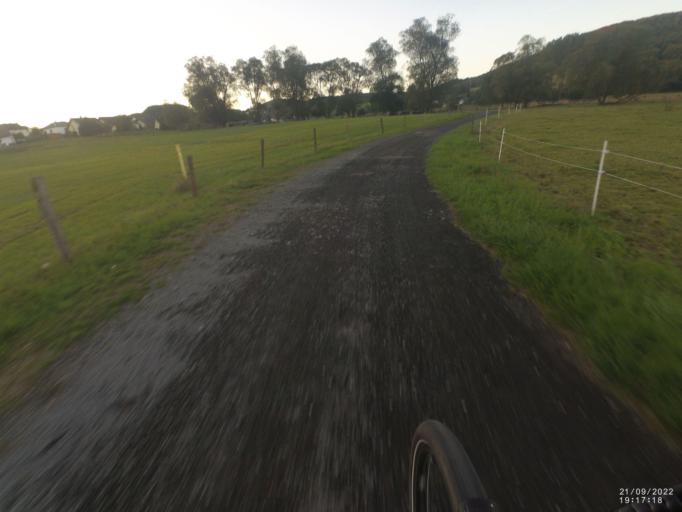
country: DE
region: Rheinland-Pfalz
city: Daun
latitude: 50.2075
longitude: 6.7952
